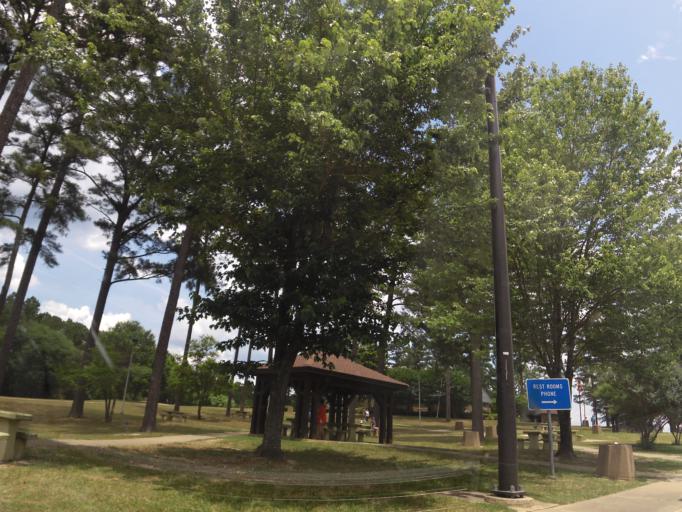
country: US
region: Alabama
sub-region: Sumter County
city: York
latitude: 32.4494
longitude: -88.3976
